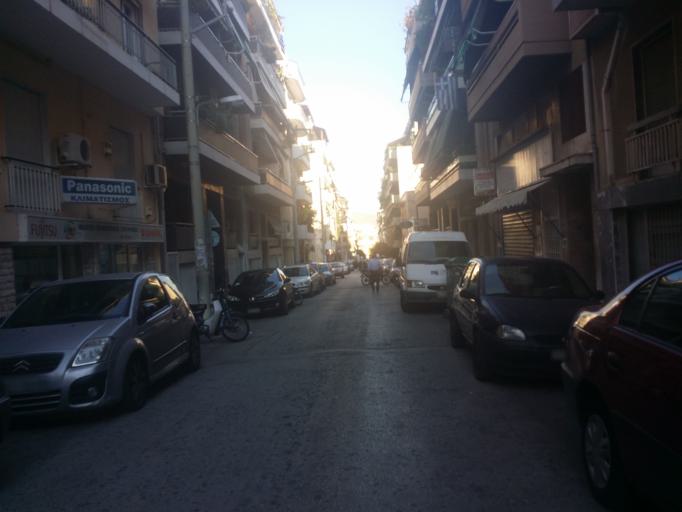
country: GR
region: Attica
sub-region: Nomarchia Athinas
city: Athens
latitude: 37.9687
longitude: 23.7069
